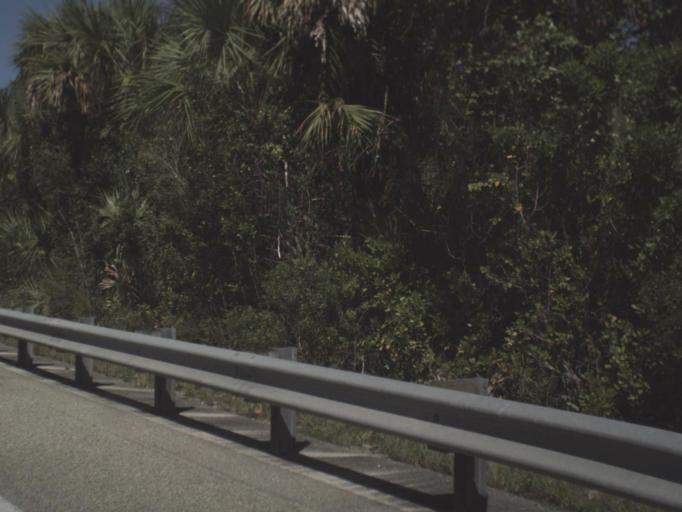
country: US
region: Florida
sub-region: Collier County
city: Marco
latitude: 25.9614
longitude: -81.5179
